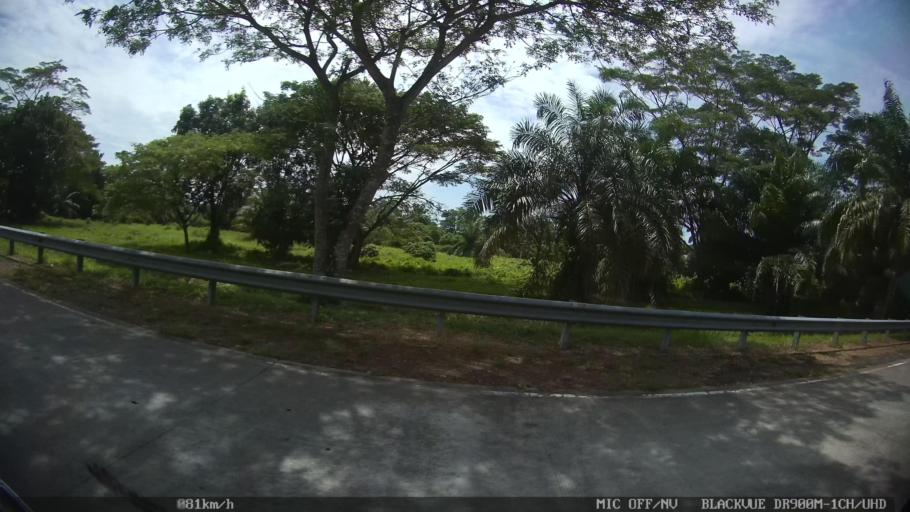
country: ID
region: North Sumatra
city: Percut
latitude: 3.6168
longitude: 98.8607
